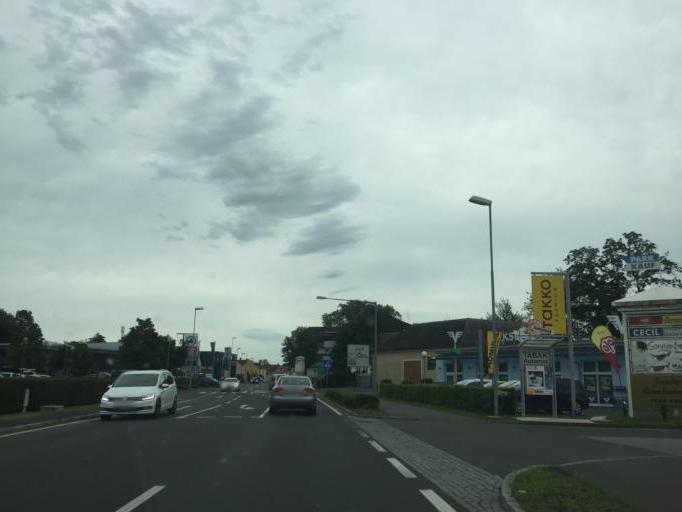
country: AT
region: Styria
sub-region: Politischer Bezirk Suedoststeiermark
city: Bad Radkersburg
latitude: 46.6910
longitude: 15.9838
